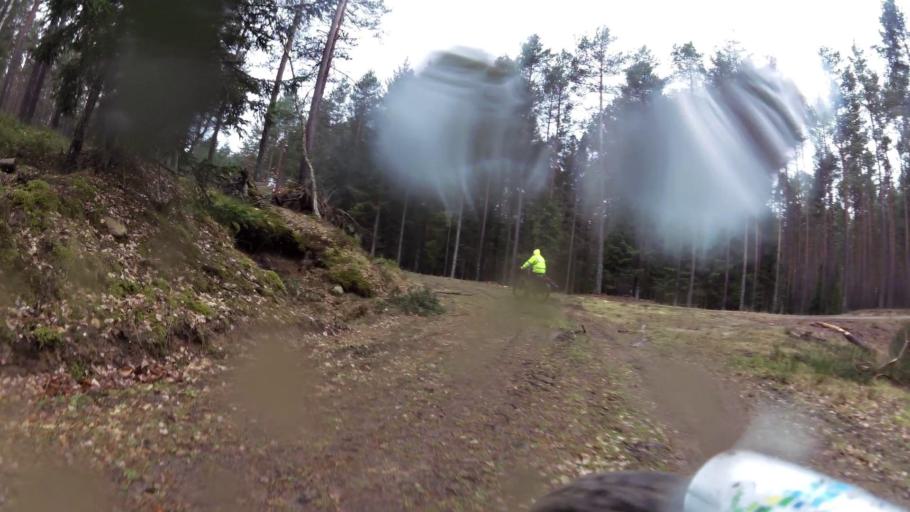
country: PL
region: Pomeranian Voivodeship
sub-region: Powiat bytowski
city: Trzebielino
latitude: 54.0778
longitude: 17.0965
